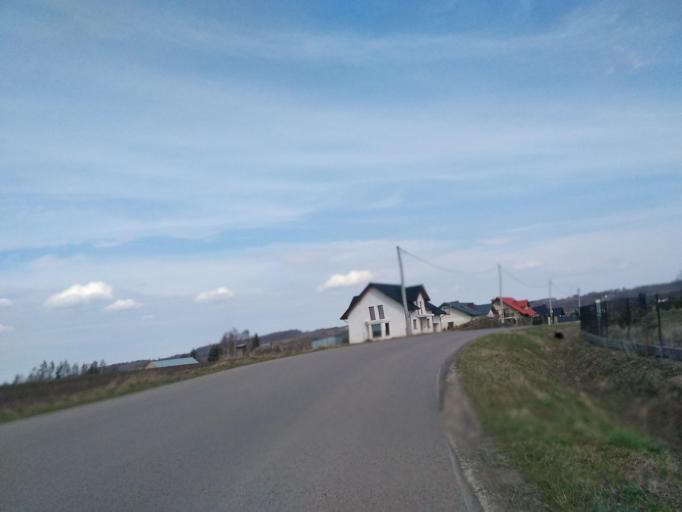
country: PL
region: Subcarpathian Voivodeship
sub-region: Powiat ropczycko-sedziszowski
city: Iwierzyce
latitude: 50.0159
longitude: 21.7847
